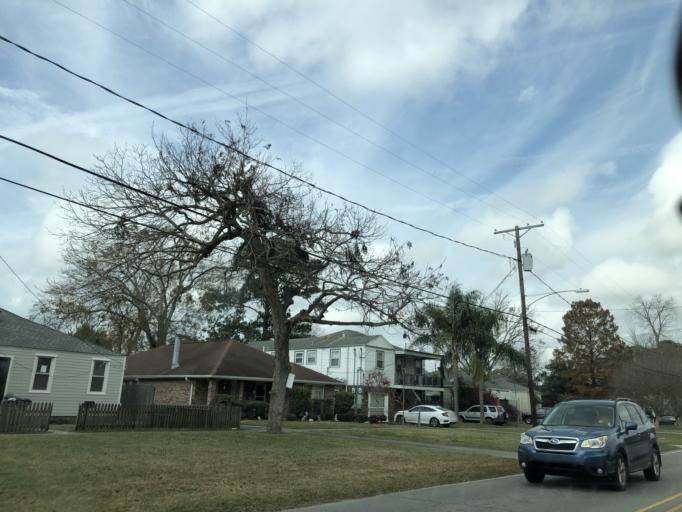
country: US
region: Louisiana
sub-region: Jefferson Parish
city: Metairie Terrace
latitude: 29.9774
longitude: -90.1605
